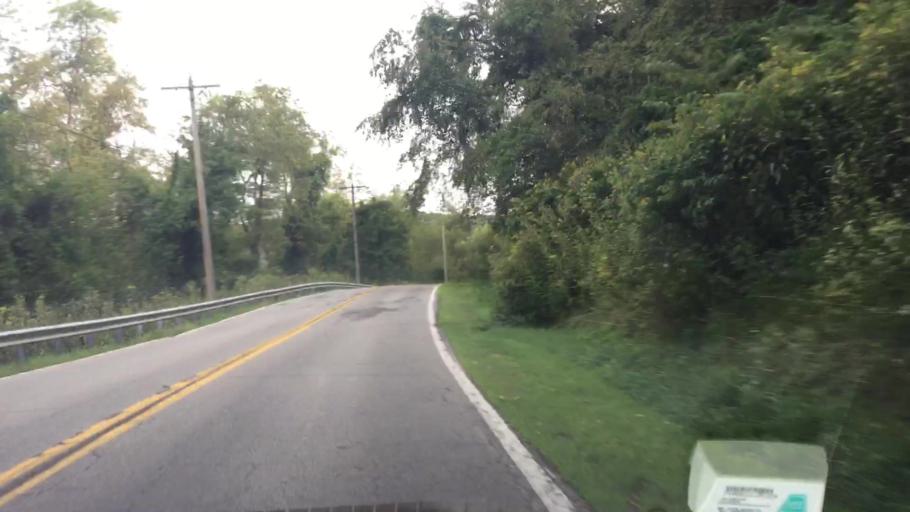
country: US
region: Pennsylvania
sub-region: Allegheny County
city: Gibsonia
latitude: 40.6002
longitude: -80.0132
